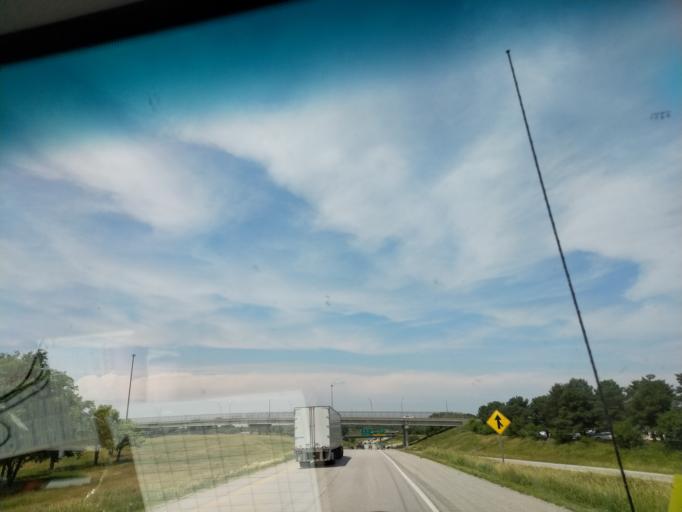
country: US
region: Iowa
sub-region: Polk County
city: Clive
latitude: 41.5932
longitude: -93.7734
